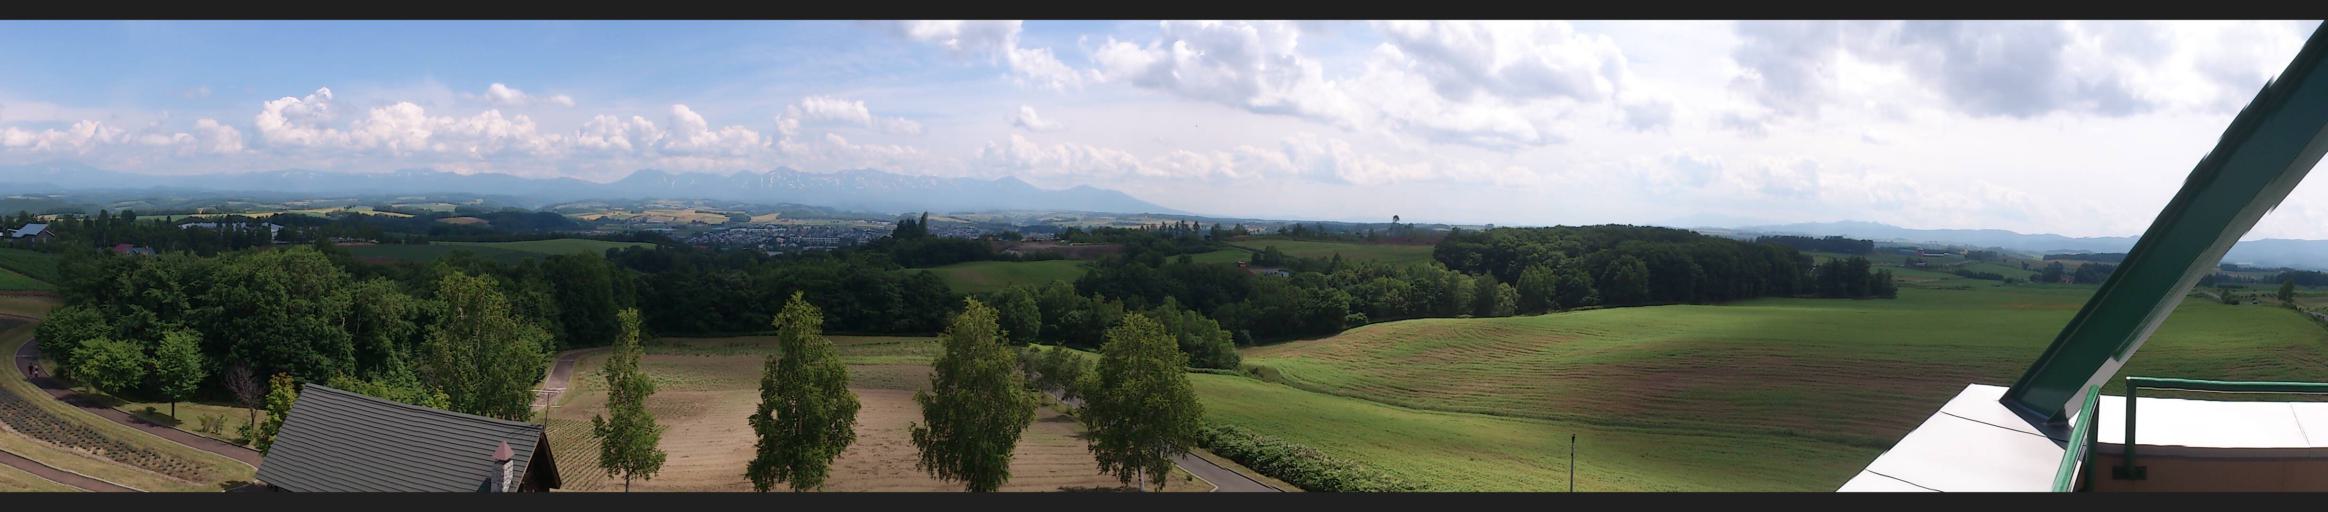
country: JP
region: Hokkaido
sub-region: Asahikawa-shi
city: Asahikawa
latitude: 43.6053
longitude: 142.4567
